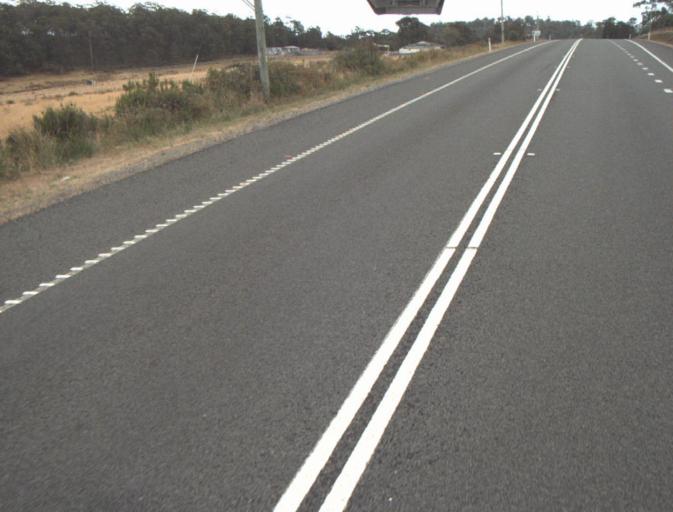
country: AU
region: Tasmania
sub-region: Launceston
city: Mayfield
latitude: -41.2513
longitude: 147.0221
